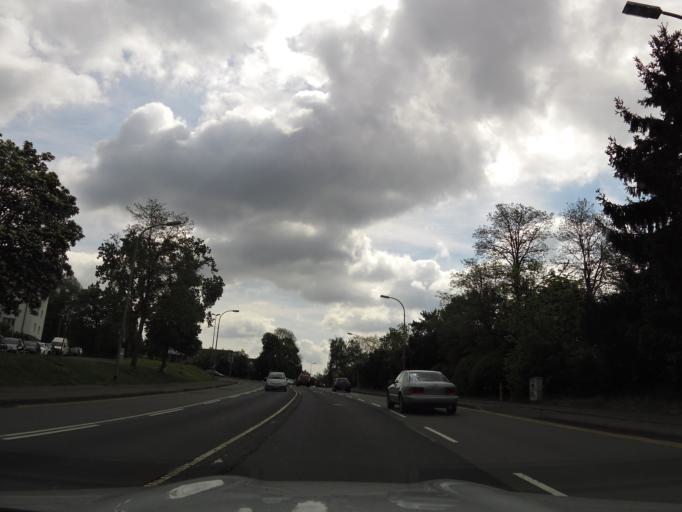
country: DE
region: Hesse
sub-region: Regierungsbezirk Giessen
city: Wetzlar
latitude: 50.5477
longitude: 8.5249
